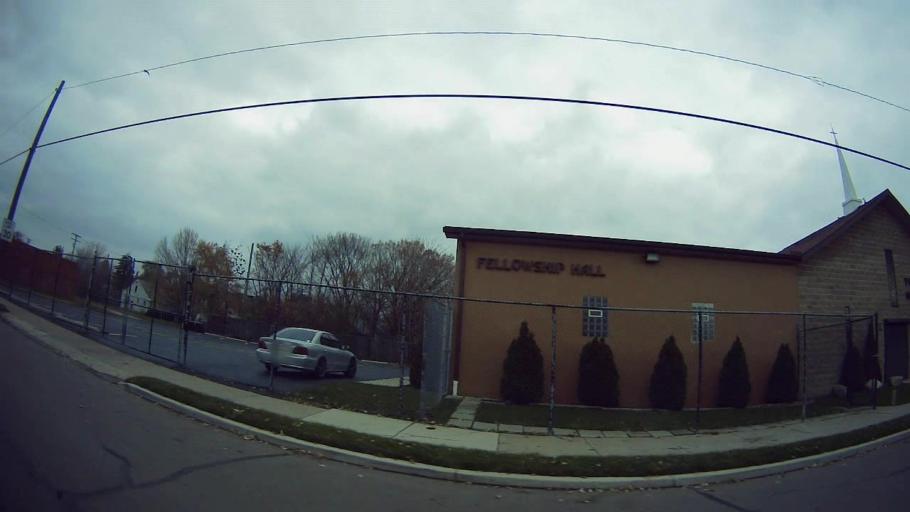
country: US
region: Michigan
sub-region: Macomb County
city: Eastpointe
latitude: 42.4391
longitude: -82.9853
